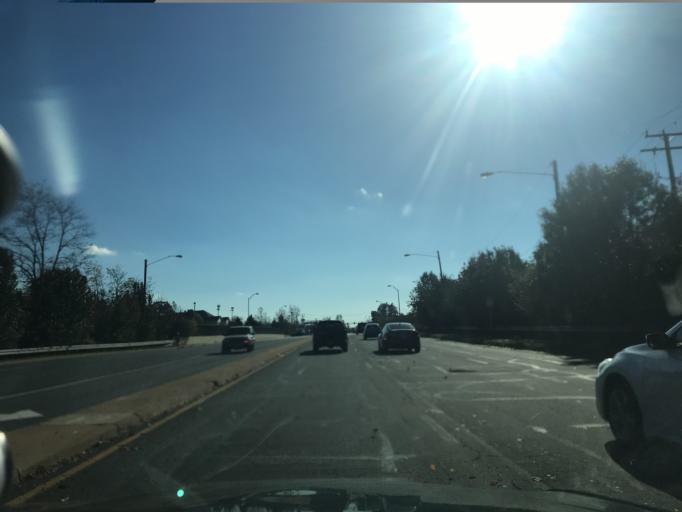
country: US
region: Virginia
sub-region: Fairfax County
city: Greenbriar
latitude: 38.8591
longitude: -77.3714
